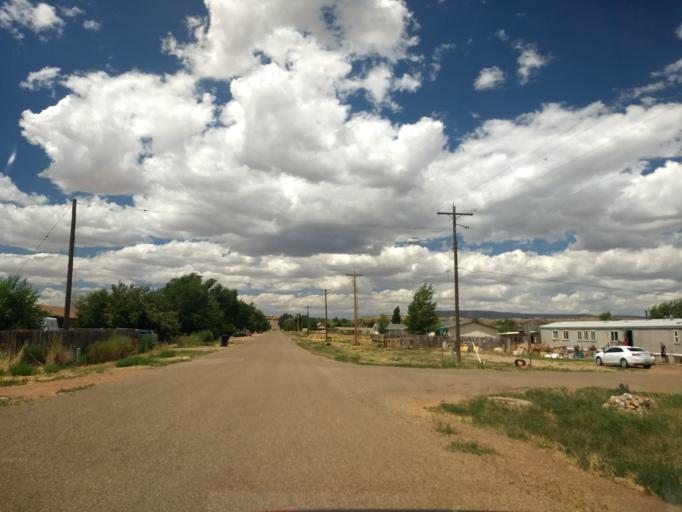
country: US
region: Arizona
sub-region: Coconino County
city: Fredonia
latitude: 36.9456
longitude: -112.5186
